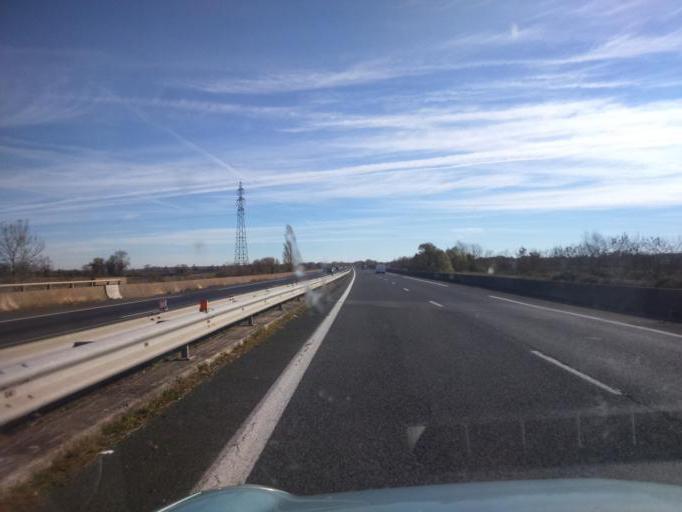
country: FR
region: Poitou-Charentes
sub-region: Departement de la Charente-Maritime
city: Breuil-Magne
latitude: 45.9575
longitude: -0.9328
